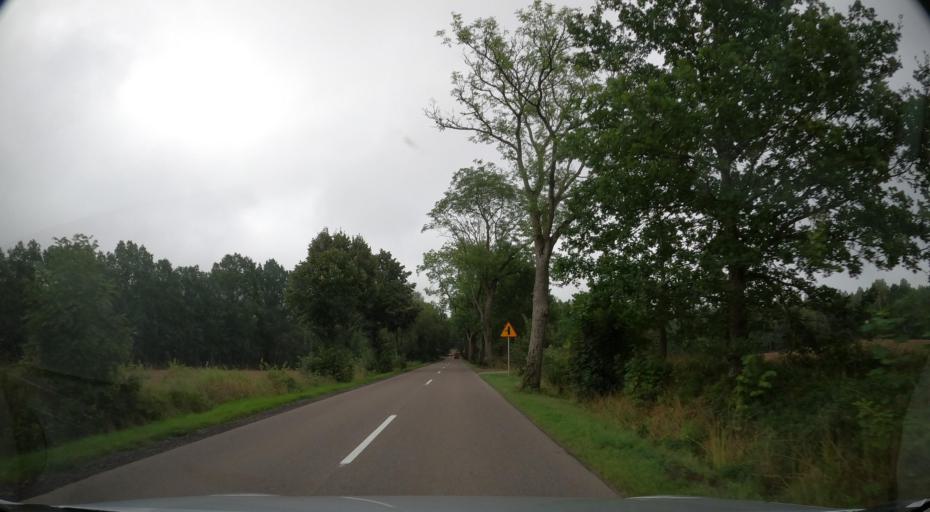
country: PL
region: Pomeranian Voivodeship
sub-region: Powiat wejherowski
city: Linia
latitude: 54.4605
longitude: 18.0463
